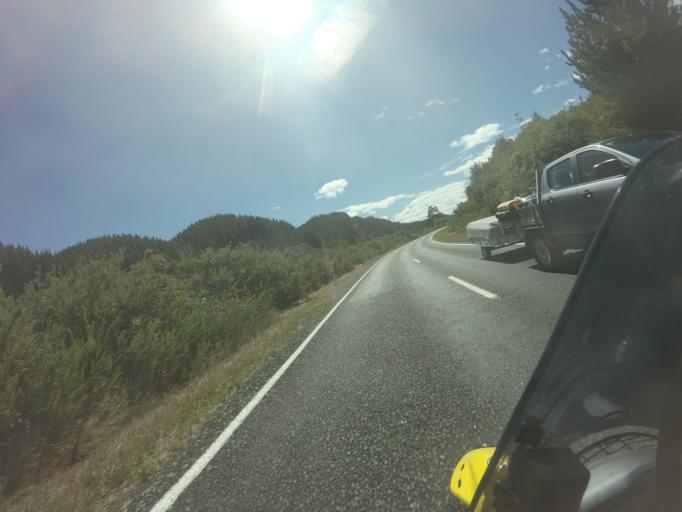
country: NZ
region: Bay of Plenty
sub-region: Kawerau District
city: Kawerau
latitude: -38.2586
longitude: 176.8194
